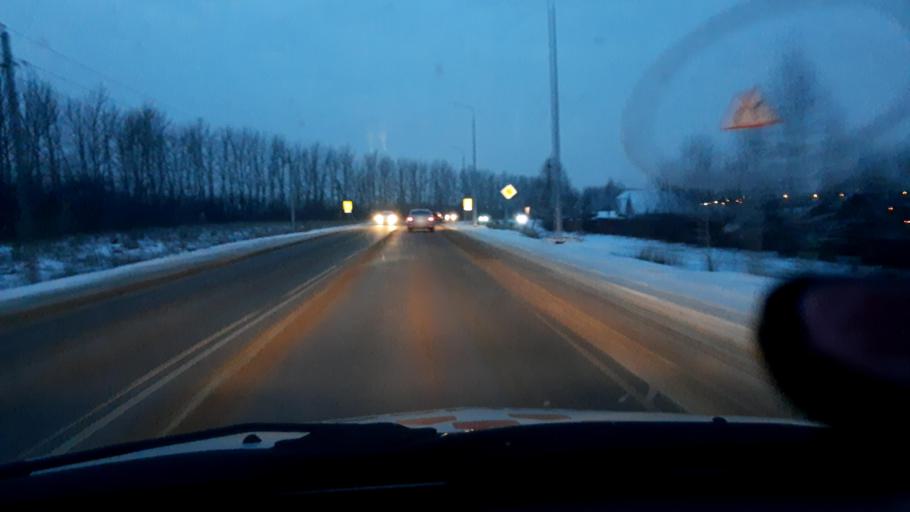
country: RU
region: Bashkortostan
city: Iglino
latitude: 54.7925
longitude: 56.2872
